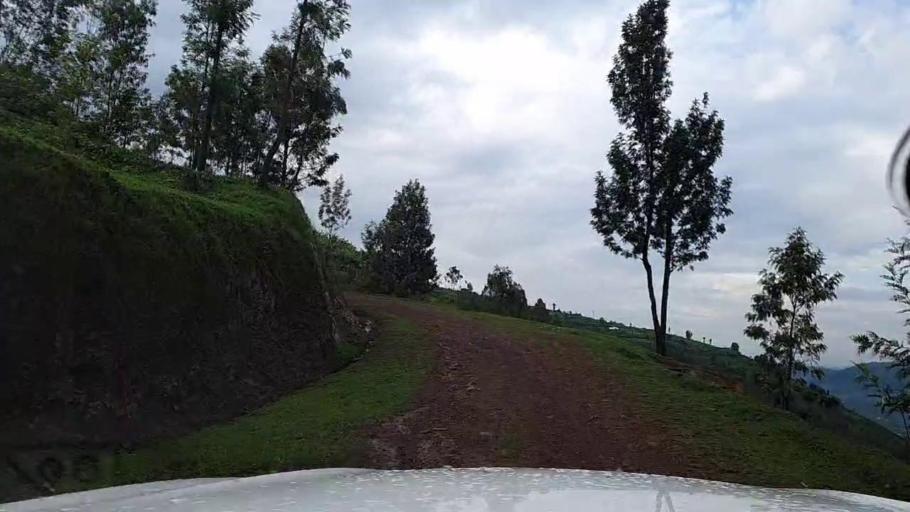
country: RW
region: Northern Province
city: Byumba
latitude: -1.7181
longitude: 29.9117
